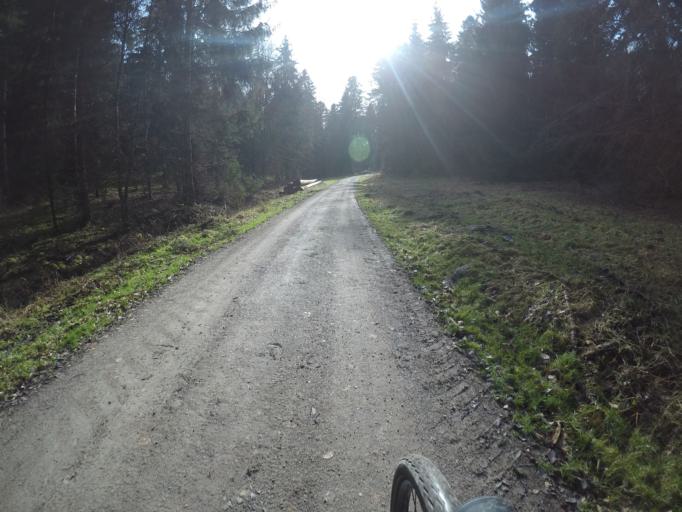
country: DE
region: Baden-Wuerttemberg
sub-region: Regierungsbezirk Stuttgart
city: Oberjettingen
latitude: 48.5934
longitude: 8.7947
